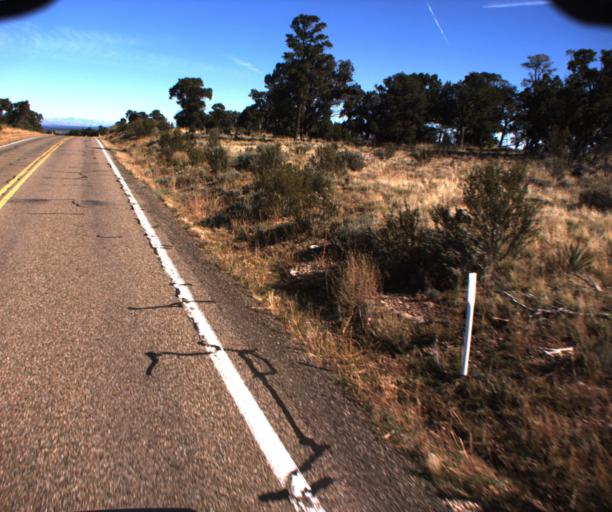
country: US
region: Arizona
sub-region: Coconino County
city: Fredonia
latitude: 36.8117
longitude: -112.2546
